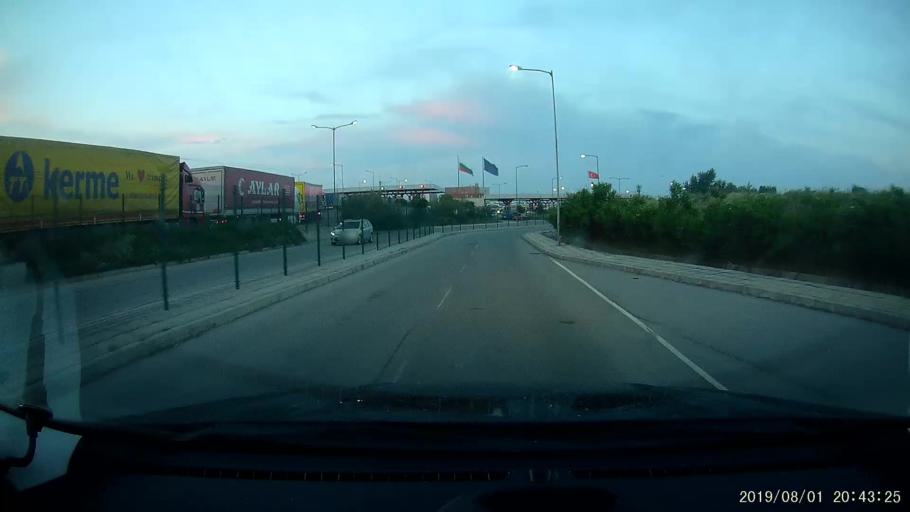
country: TR
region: Edirne
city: Lalapasa
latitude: 41.9623
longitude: 26.6033
